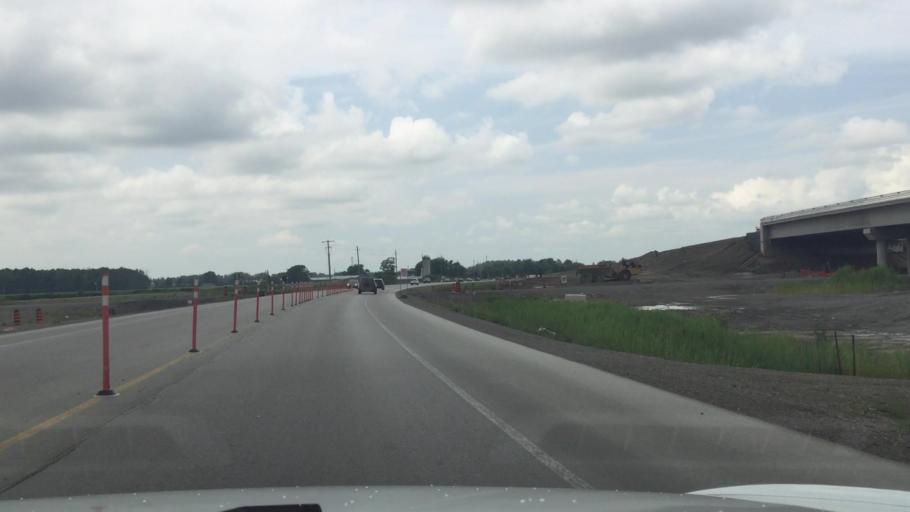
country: CA
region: Ontario
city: Oshawa
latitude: 43.9127
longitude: -78.7630
